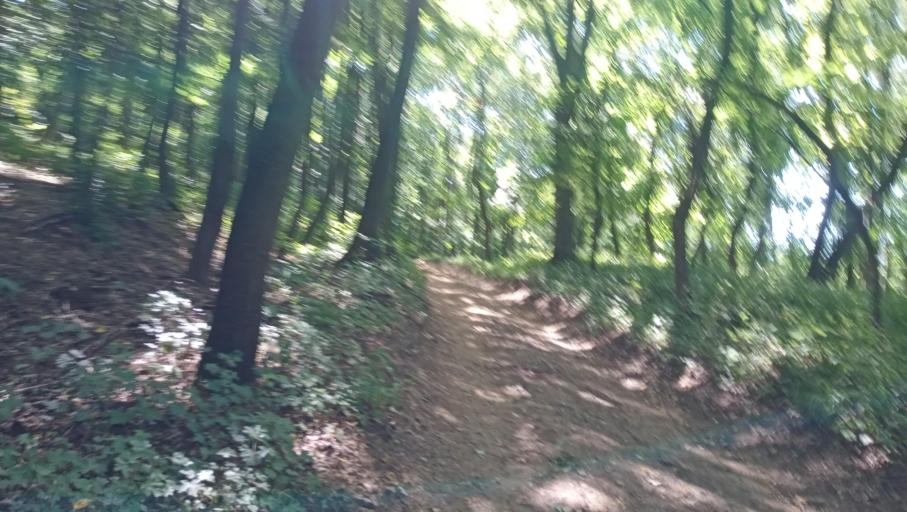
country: HU
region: Somogy
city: Siofok
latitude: 46.8268
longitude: 18.0611
